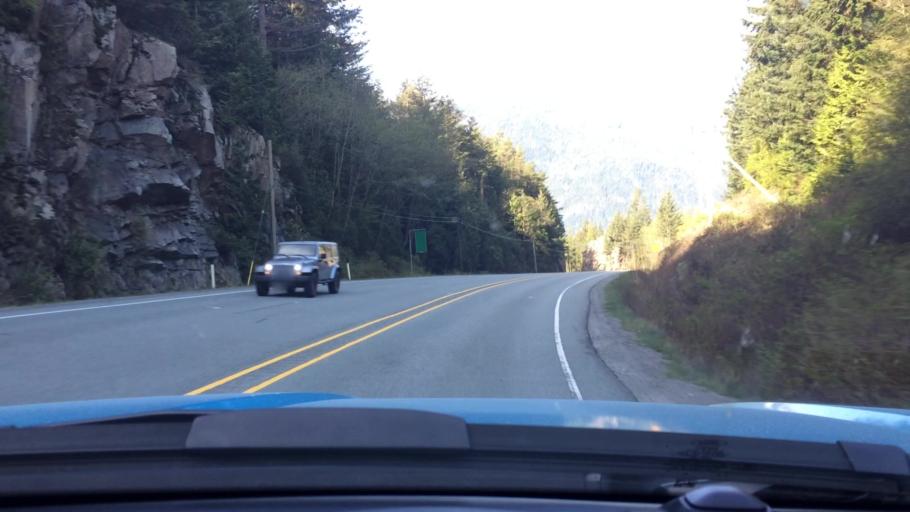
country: CA
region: British Columbia
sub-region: Greater Vancouver Regional District
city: Lions Bay
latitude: 49.6431
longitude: -123.2075
